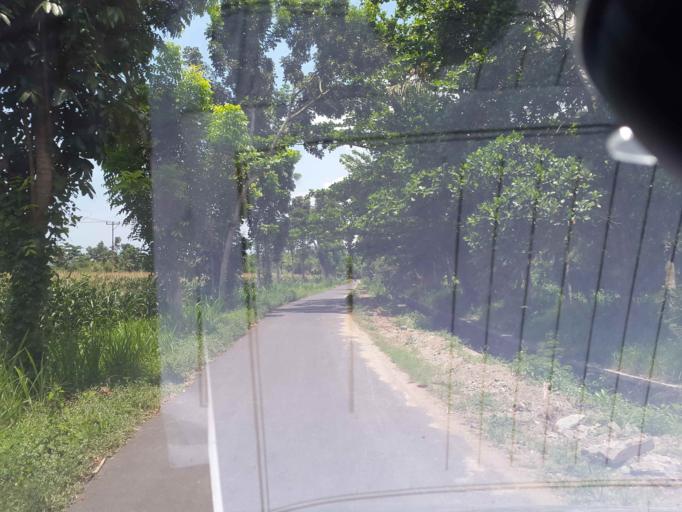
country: ID
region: West Nusa Tenggara
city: Jelateng Timur
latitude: -8.6990
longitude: 116.0811
